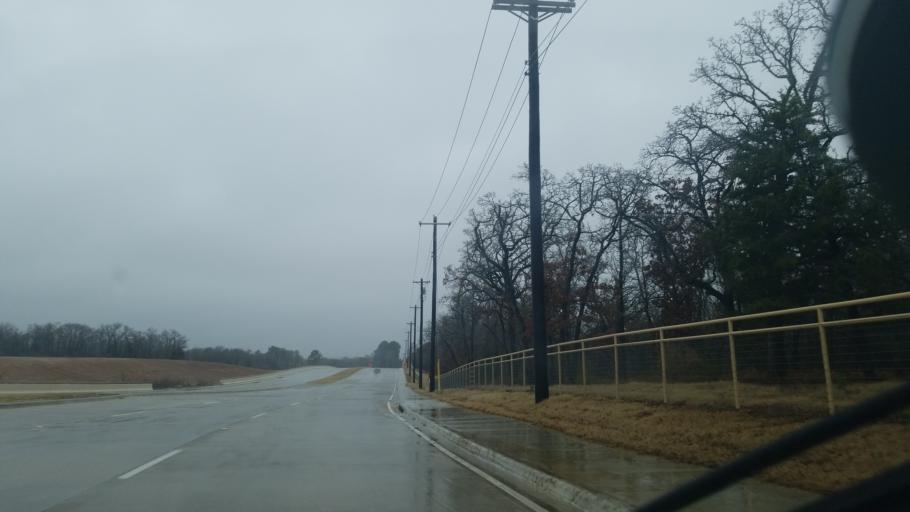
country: US
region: Texas
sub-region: Denton County
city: Corinth
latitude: 33.1423
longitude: -97.0960
